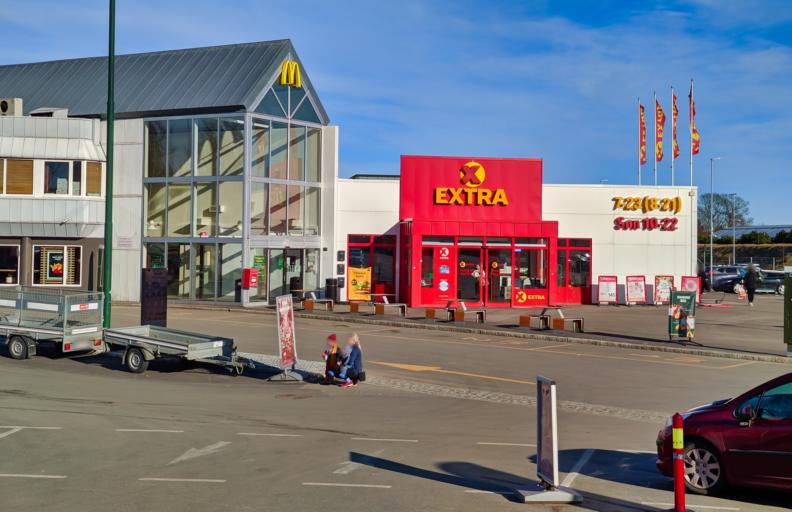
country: NO
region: Aust-Agder
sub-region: Grimstad
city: Grimstad
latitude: 58.3415
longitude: 8.5685
